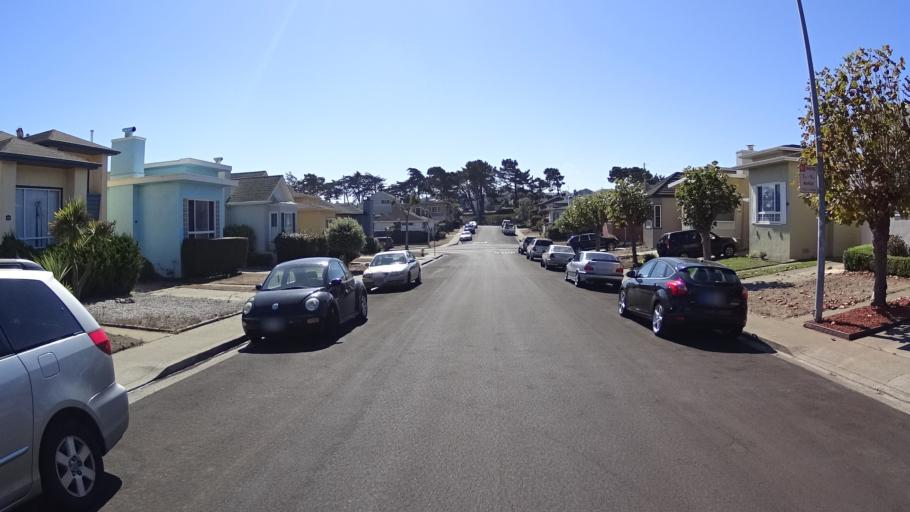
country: US
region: California
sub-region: San Mateo County
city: Broadmoor
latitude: 37.7006
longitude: -122.4927
